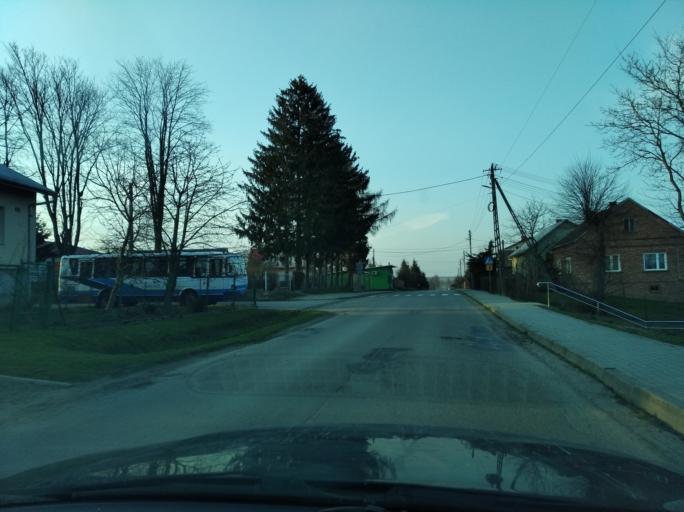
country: PL
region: Subcarpathian Voivodeship
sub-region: Powiat przeworski
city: Zarzecze
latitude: 49.9705
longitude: 22.5529
